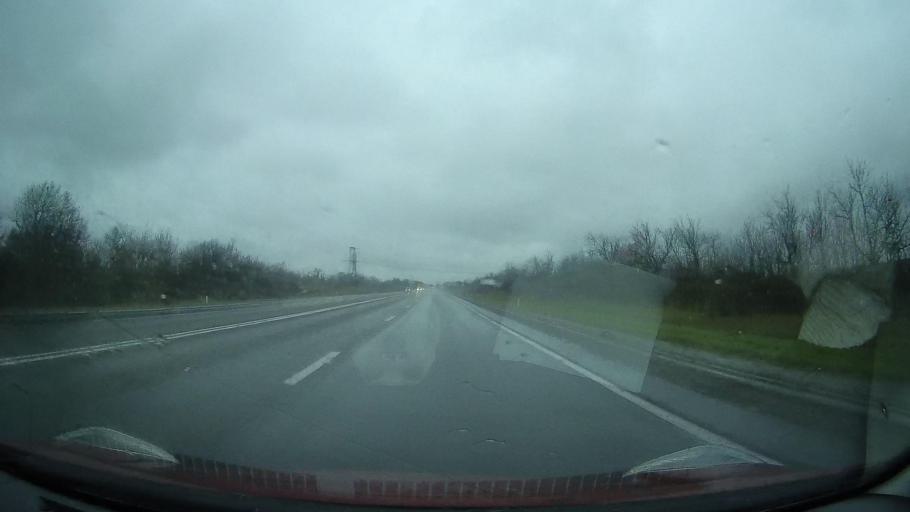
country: RU
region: Stavropol'skiy
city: Nevinnomyssk
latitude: 44.6335
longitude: 42.0115
